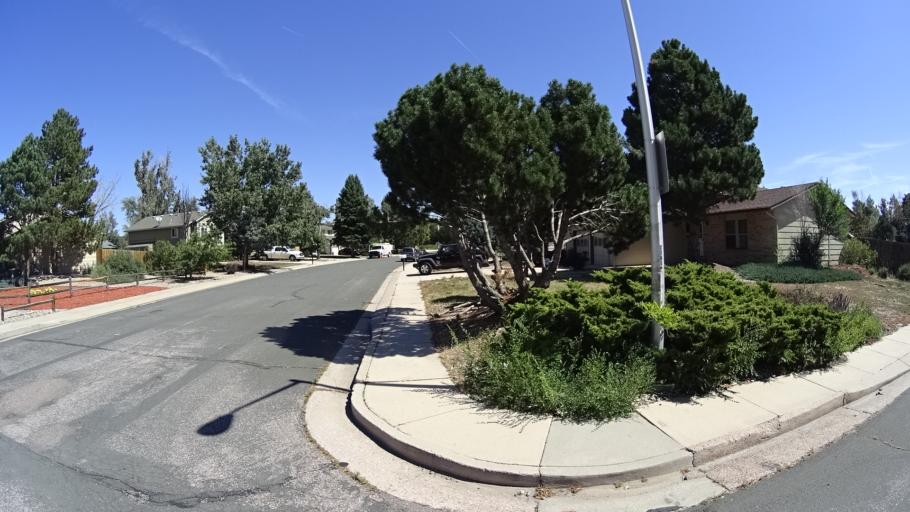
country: US
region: Colorado
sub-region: El Paso County
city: Black Forest
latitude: 38.9427
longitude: -104.7614
